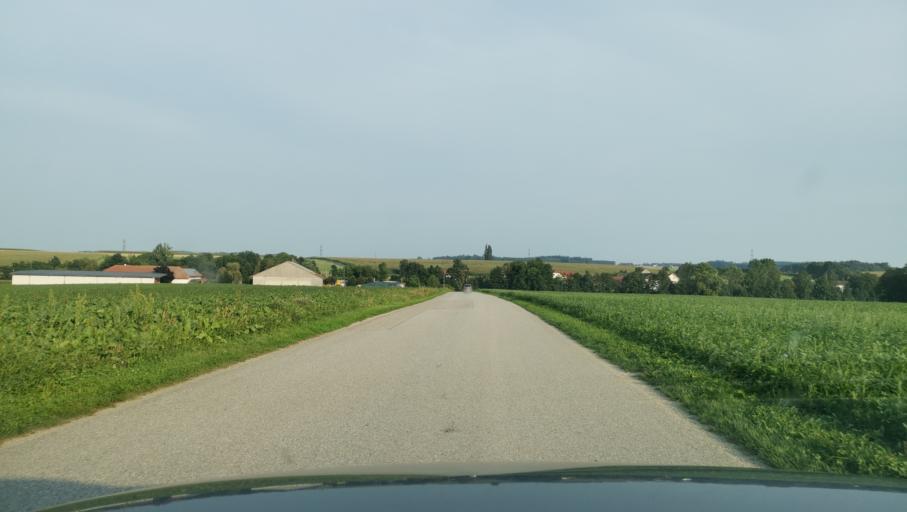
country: AT
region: Upper Austria
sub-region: Politischer Bezirk Grieskirchen
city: Grieskirchen
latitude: 48.2901
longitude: 13.8052
